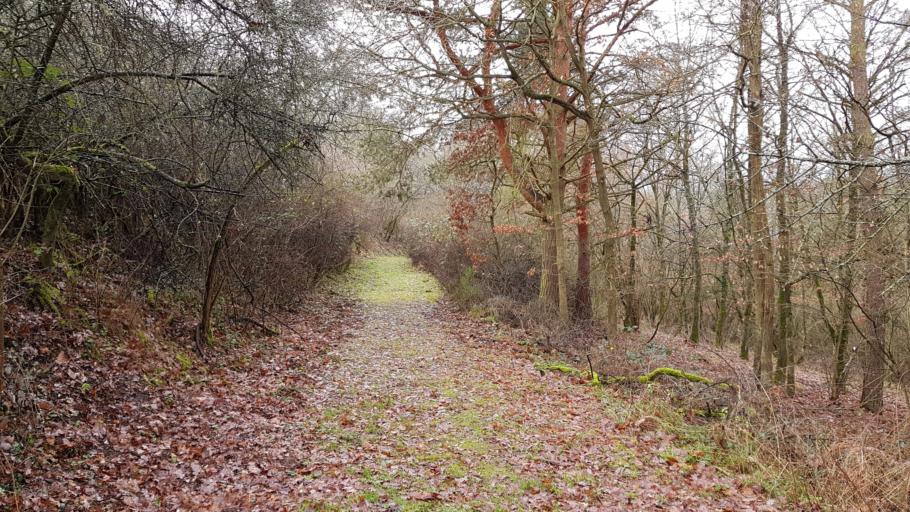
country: DE
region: Rheinland-Pfalz
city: Oberwesel
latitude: 50.0936
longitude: 7.7179
